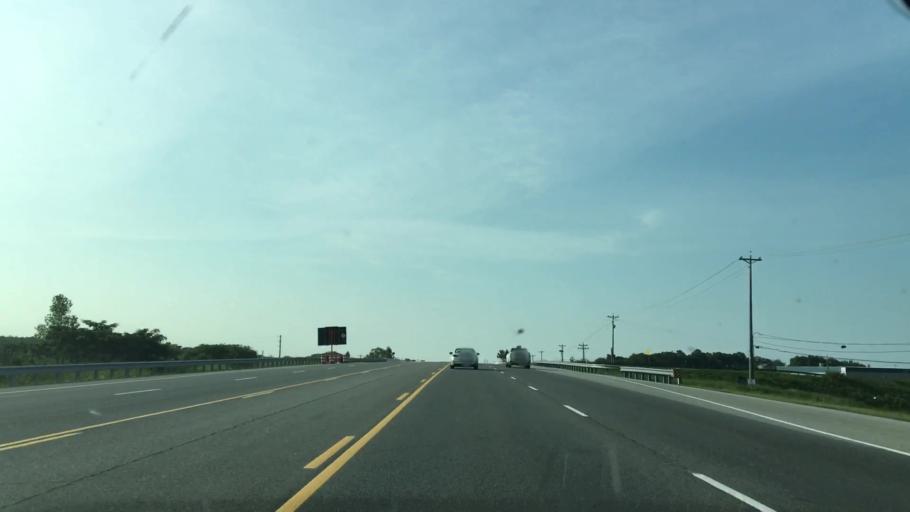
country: US
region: Tennessee
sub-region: Wilson County
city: Mount Juliet
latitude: 36.2287
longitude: -86.4274
